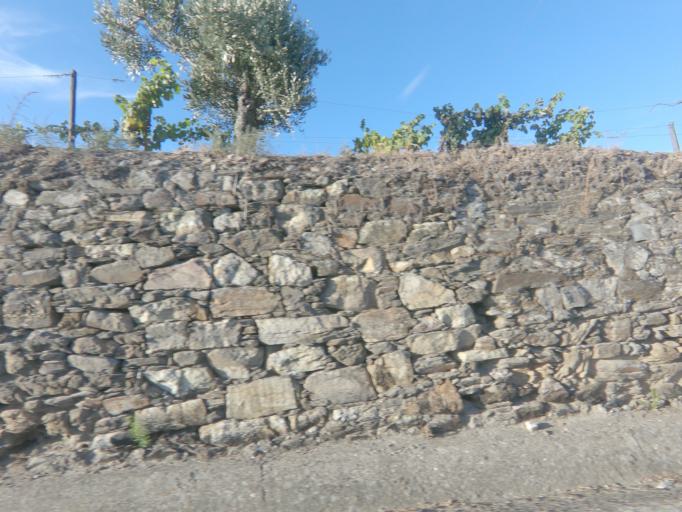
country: PT
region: Vila Real
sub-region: Peso da Regua
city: Godim
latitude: 41.1607
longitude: -7.8165
